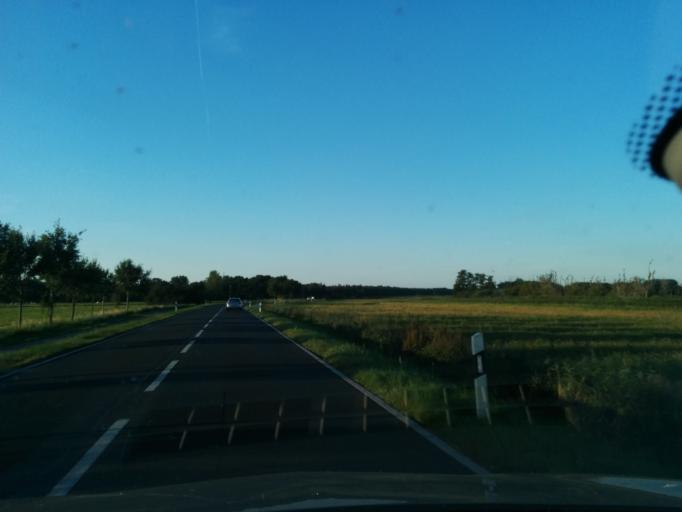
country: DE
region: Mecklenburg-Vorpommern
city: Seebad Bansin
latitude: 53.9726
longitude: 14.0726
